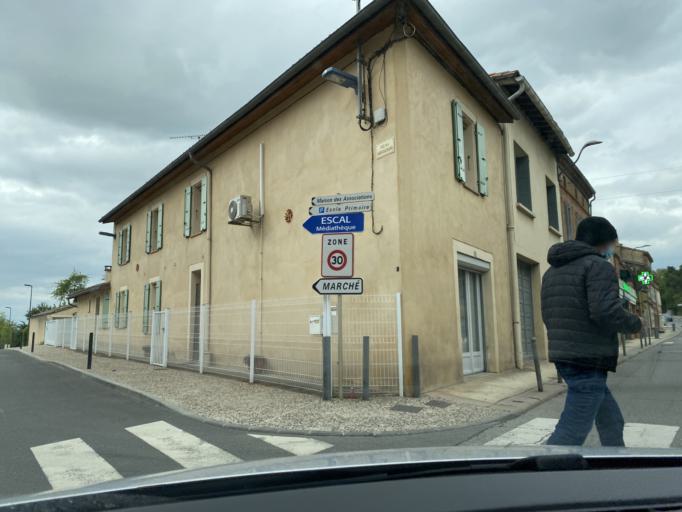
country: FR
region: Midi-Pyrenees
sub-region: Departement de la Haute-Garonne
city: Nailloux
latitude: 43.3585
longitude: 1.6238
